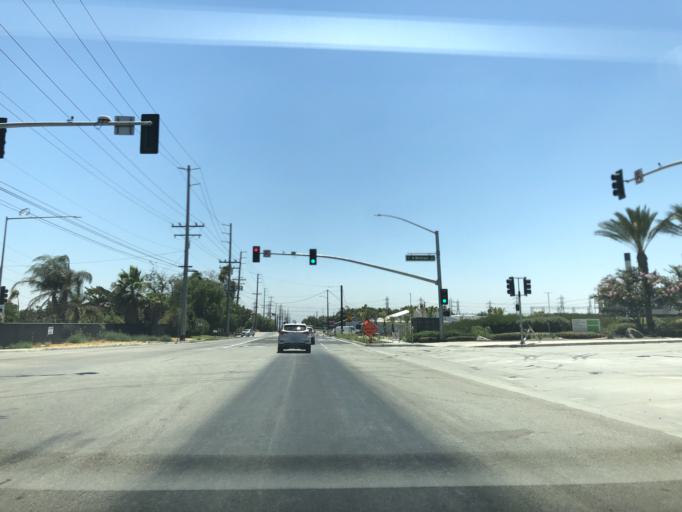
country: US
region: California
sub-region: San Bernardino County
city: Rancho Cucamonga
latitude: 34.0948
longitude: -117.5239
